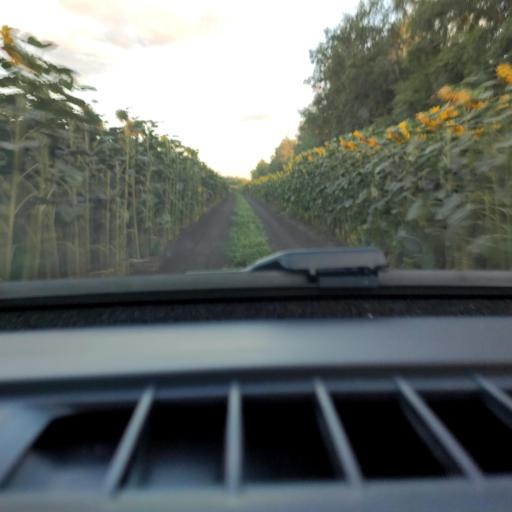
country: RU
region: Voronezj
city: Verkhnyaya Khava
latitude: 51.6012
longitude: 39.8395
